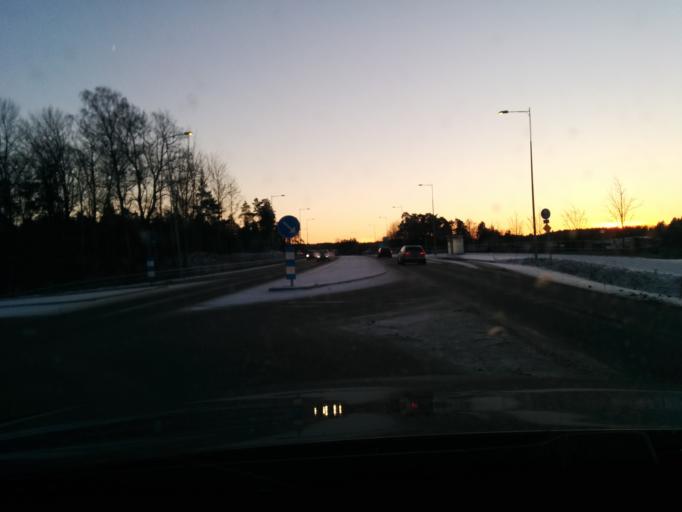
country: SE
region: Stockholm
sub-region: Taby Kommun
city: Taby
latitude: 59.4771
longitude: 18.0530
